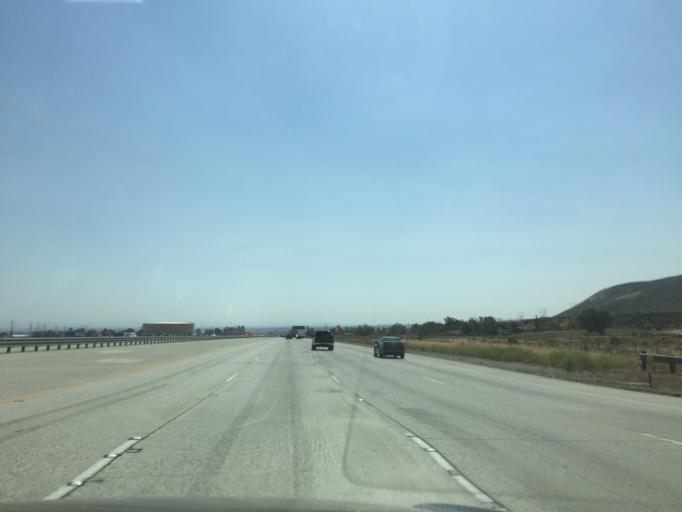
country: US
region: California
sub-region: San Bernardino County
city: Fontana
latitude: 34.1753
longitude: -117.4464
